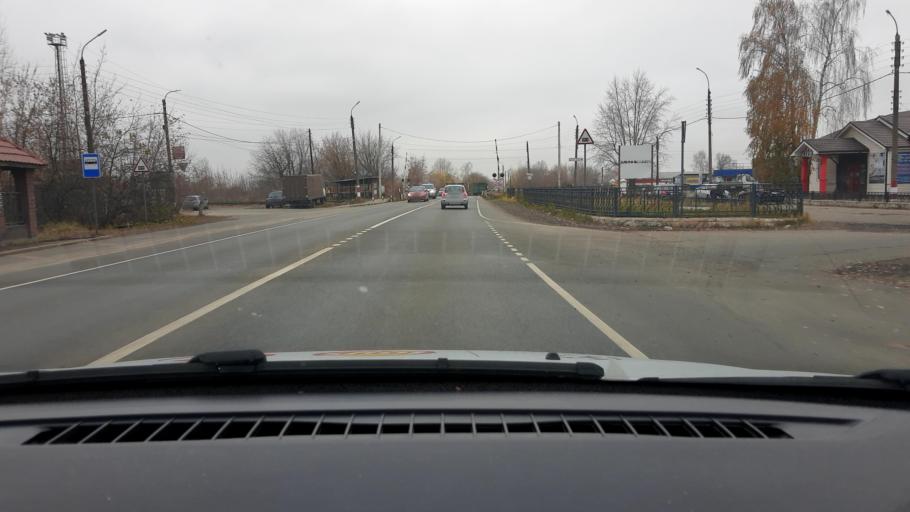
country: RU
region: Nizjnij Novgorod
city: Gidrotorf
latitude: 56.5271
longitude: 43.5514
